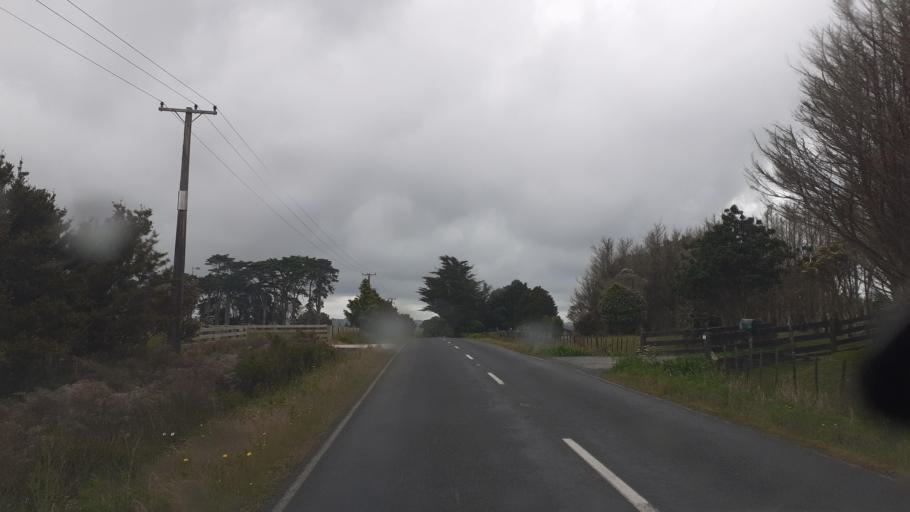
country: NZ
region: Northland
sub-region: Far North District
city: Waimate North
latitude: -35.2780
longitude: 173.8308
